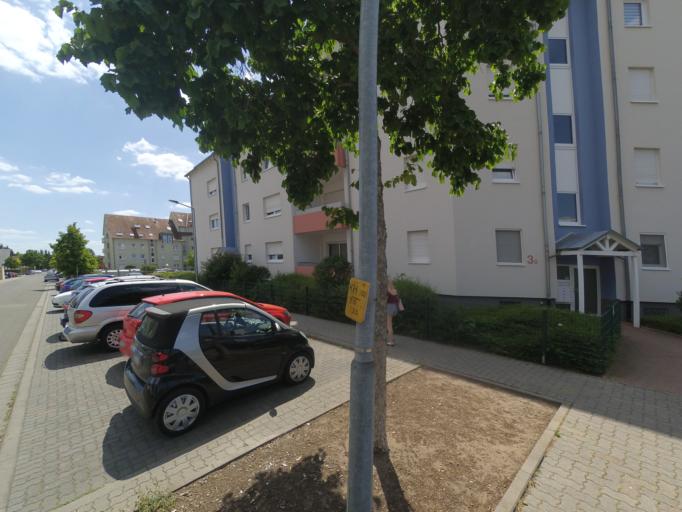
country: DE
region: Rheinland-Pfalz
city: Frankenthal
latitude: 49.5210
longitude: 8.3582
